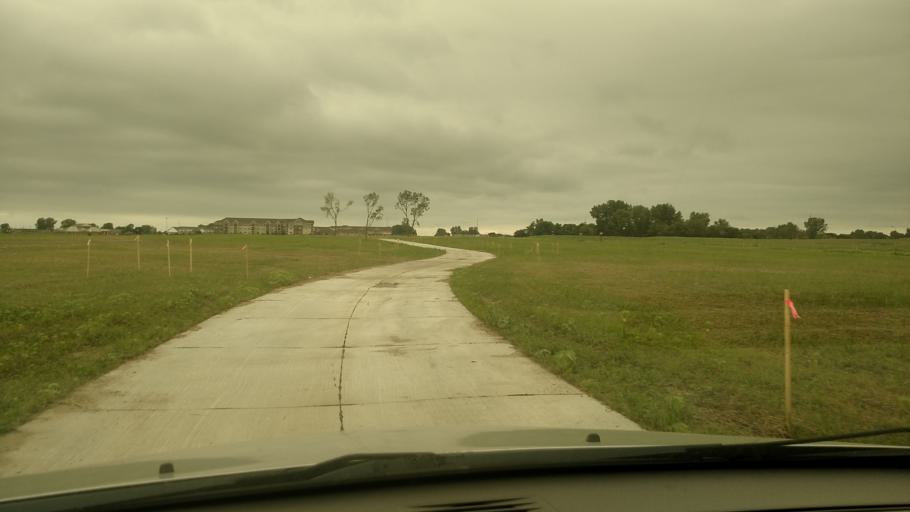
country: US
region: Iowa
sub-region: Polk County
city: Ankeny
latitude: 41.7130
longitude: -93.6116
